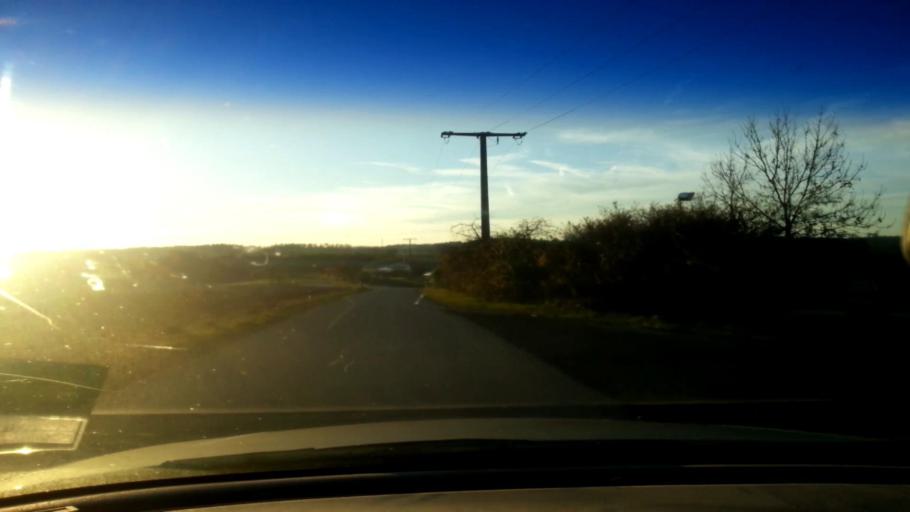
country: DE
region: Bavaria
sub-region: Upper Franconia
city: Heiligenstadt
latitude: 49.8395
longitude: 11.1640
